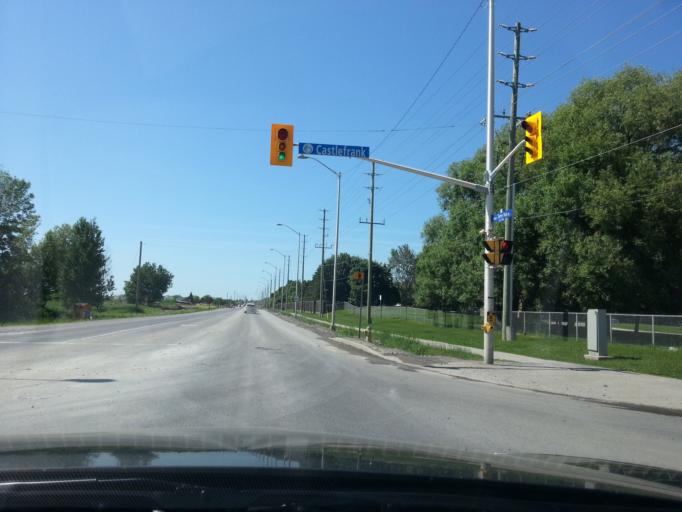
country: CA
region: Ontario
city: Bells Corners
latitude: 45.2849
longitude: -75.8856
